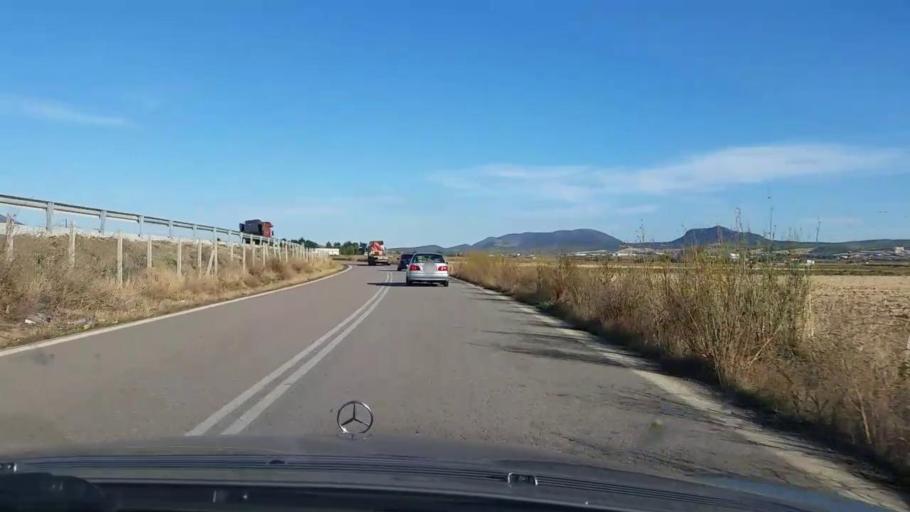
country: GR
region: Central Greece
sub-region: Nomos Voiotias
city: Thivai
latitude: 38.3645
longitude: 23.3134
